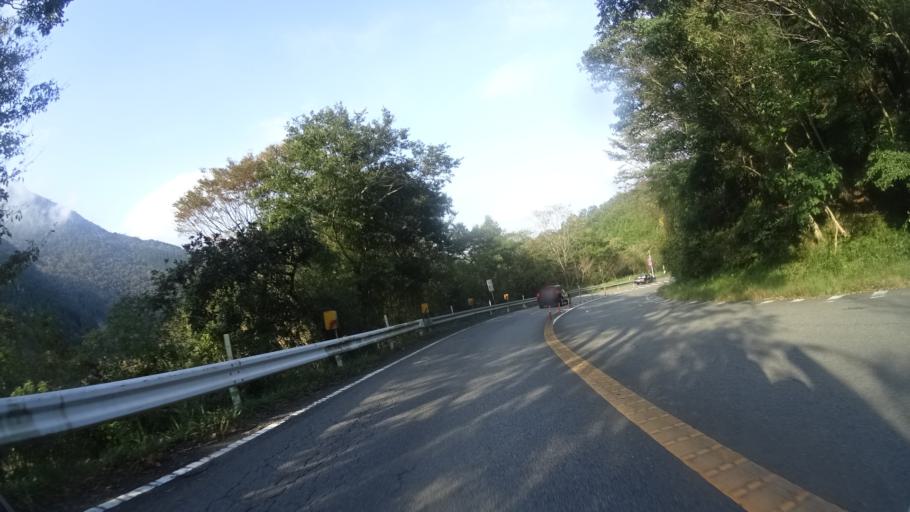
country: JP
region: Oita
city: Beppu
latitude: 33.2712
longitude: 131.4443
